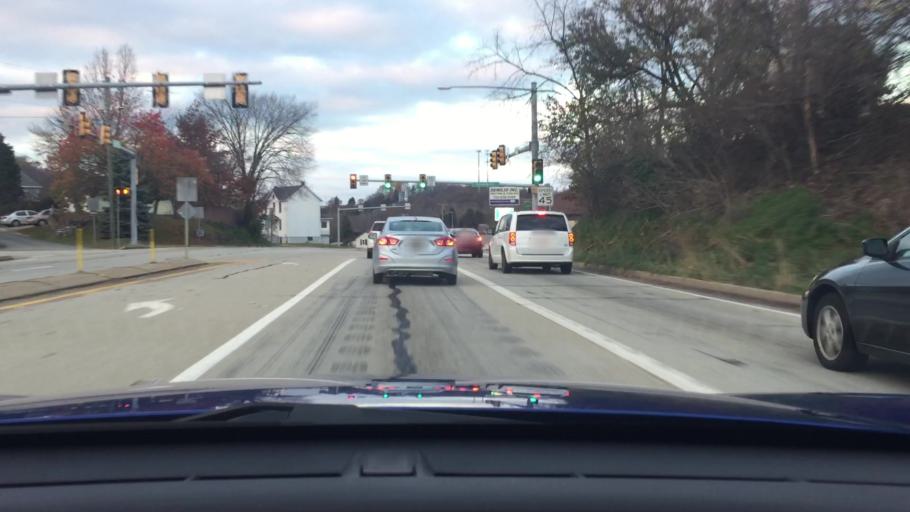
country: US
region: Pennsylvania
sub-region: Westmoreland County
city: South Greensburg
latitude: 40.2733
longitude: -79.5555
